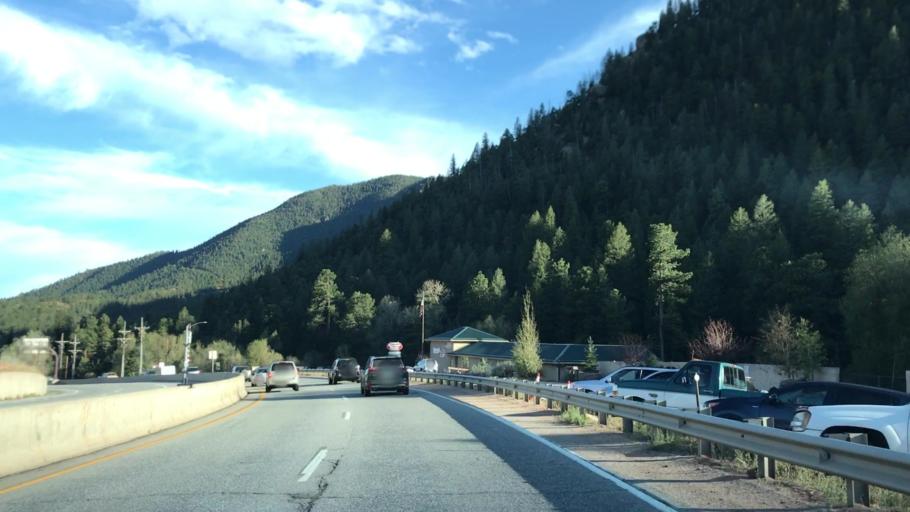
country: US
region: Colorado
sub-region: El Paso County
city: Cascade-Chipita Park
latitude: 38.8962
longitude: -104.9712
